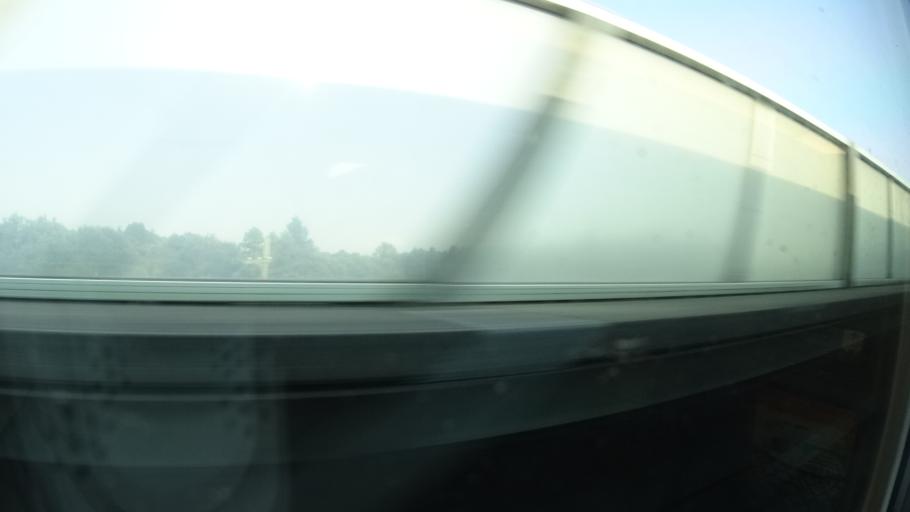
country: JP
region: Tochigi
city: Oyama
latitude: 36.2571
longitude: 139.7695
